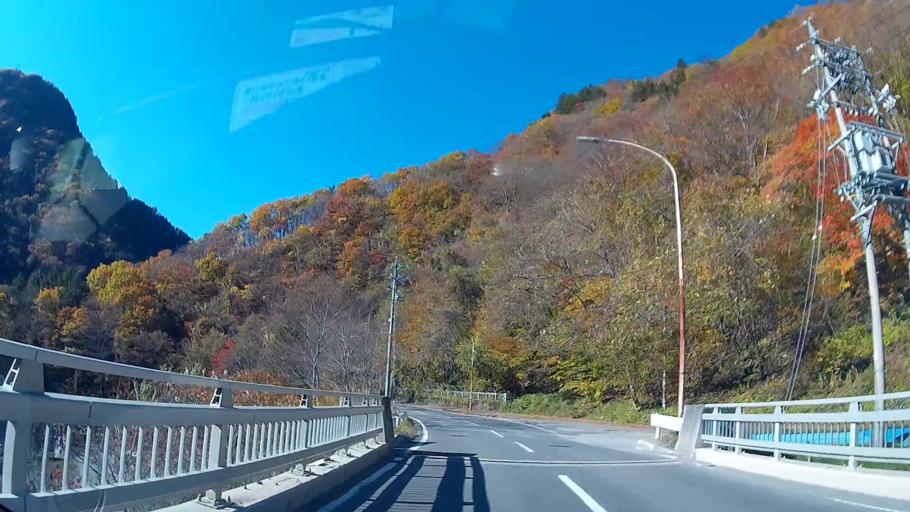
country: JP
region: Nagano
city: Toyoshina
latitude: 36.1593
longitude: 137.6749
